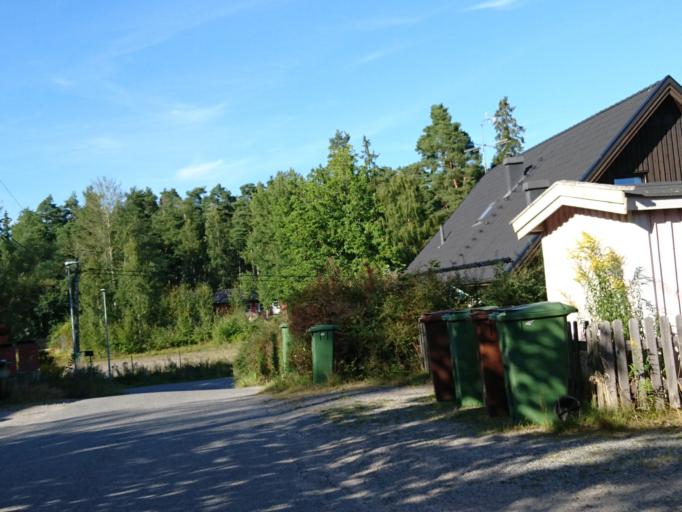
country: SE
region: Stockholm
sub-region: Huddinge Kommun
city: Segeltorp
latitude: 59.2672
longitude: 17.9525
